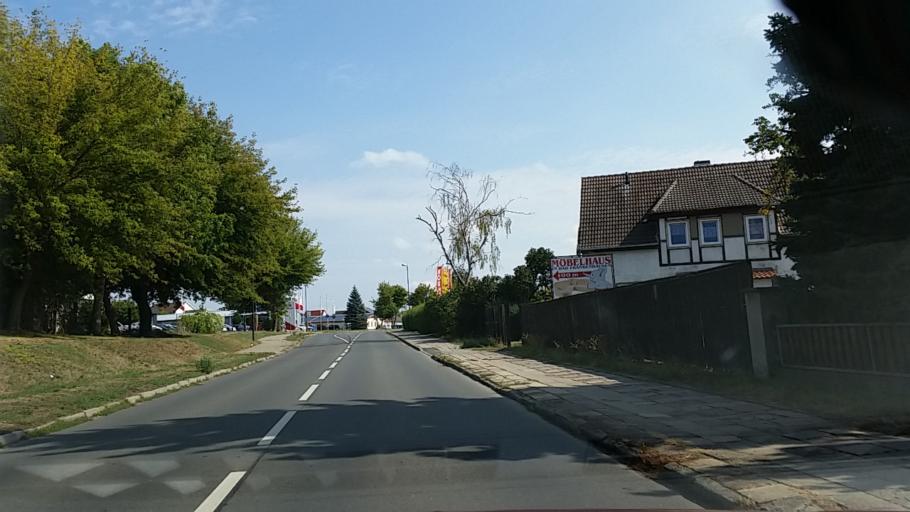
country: DE
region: Thuringia
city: Bad Frankenhausen
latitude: 51.3548
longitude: 11.1105
